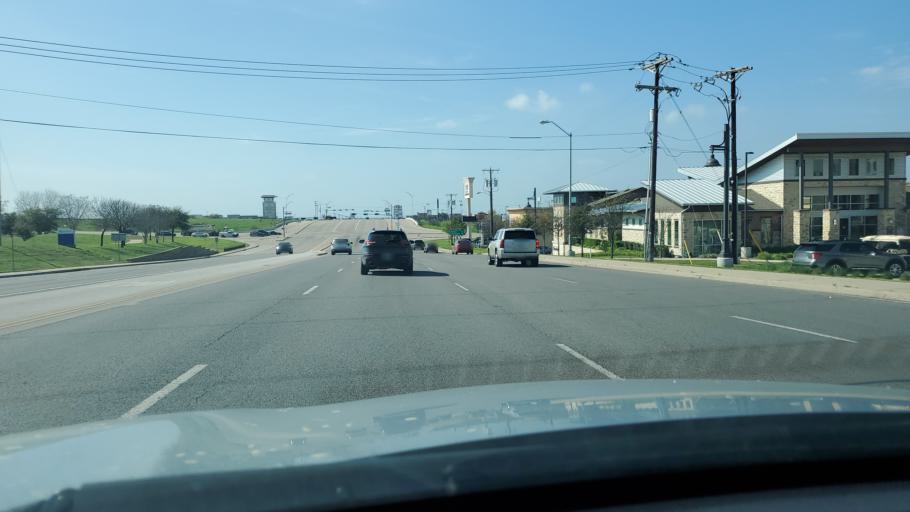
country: US
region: Texas
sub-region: Bell County
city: Temple
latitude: 31.0762
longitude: -97.3670
